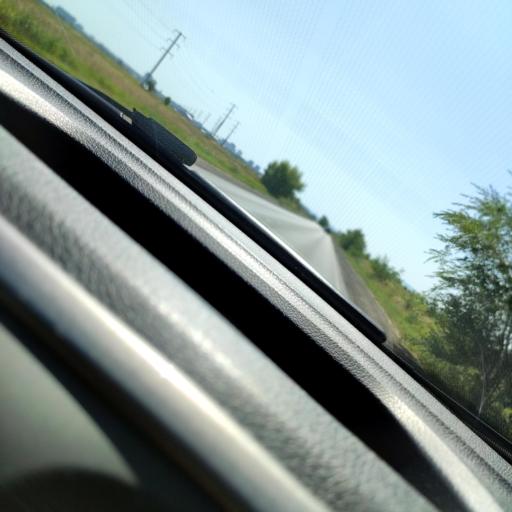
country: RU
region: Samara
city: Podstepki
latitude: 53.5203
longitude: 49.2025
